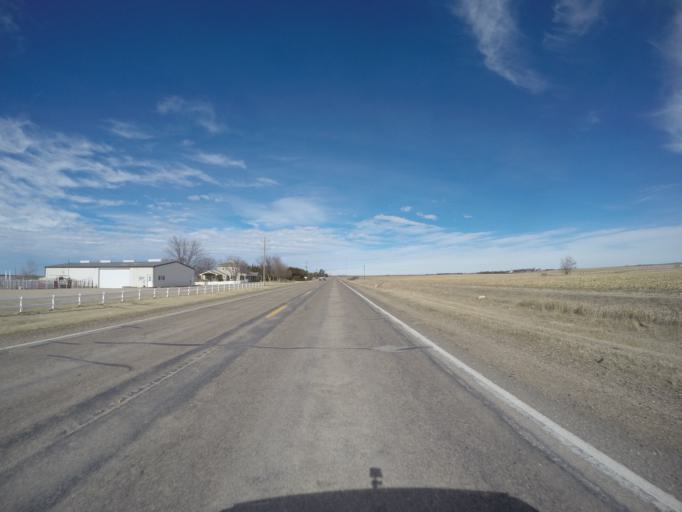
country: US
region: Nebraska
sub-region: Franklin County
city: Franklin
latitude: 40.1233
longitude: -98.9523
